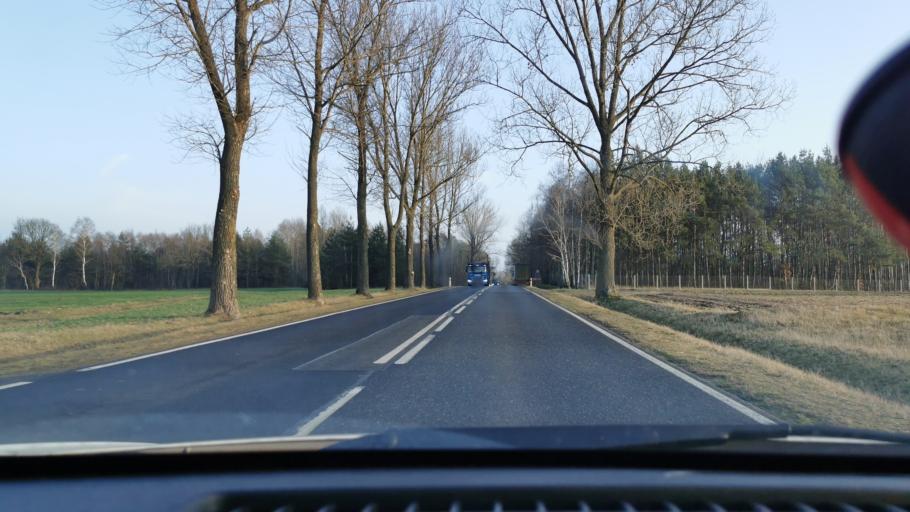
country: PL
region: Lodz Voivodeship
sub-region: Powiat laski
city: Buczek
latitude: 51.5629
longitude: 19.2072
